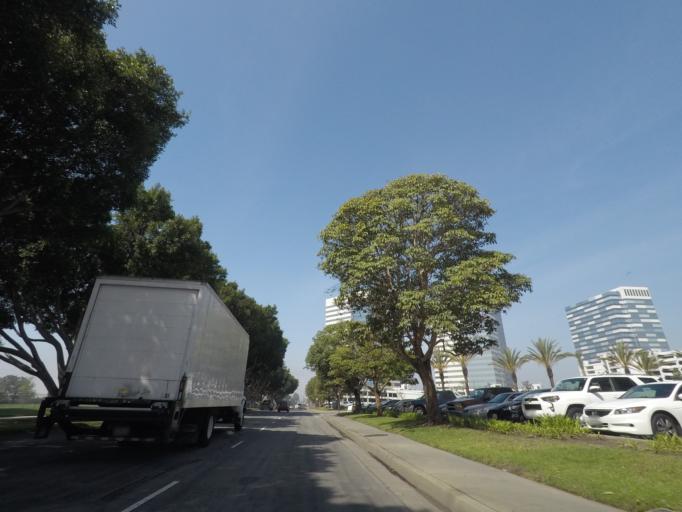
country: US
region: California
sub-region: Los Angeles County
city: Del Aire
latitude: 33.9165
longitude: -118.3921
